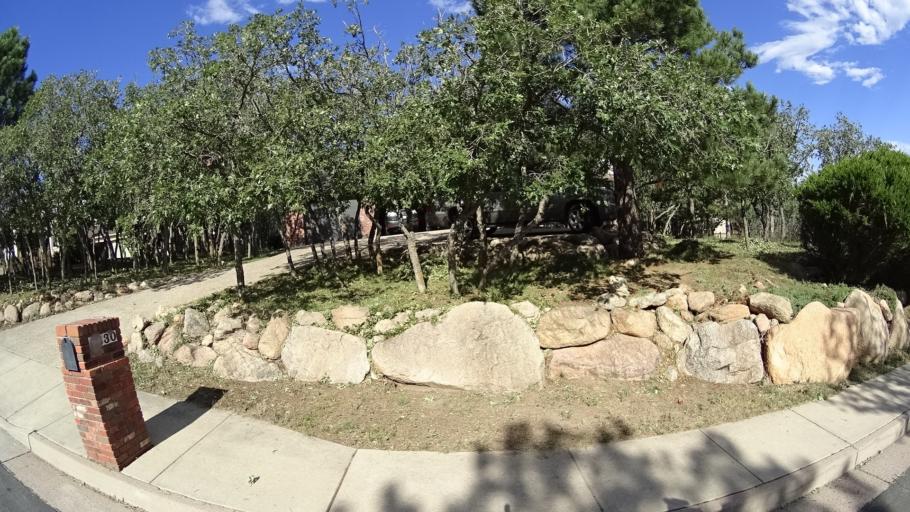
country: US
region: Colorado
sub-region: El Paso County
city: Stratmoor
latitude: 38.7692
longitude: -104.8265
